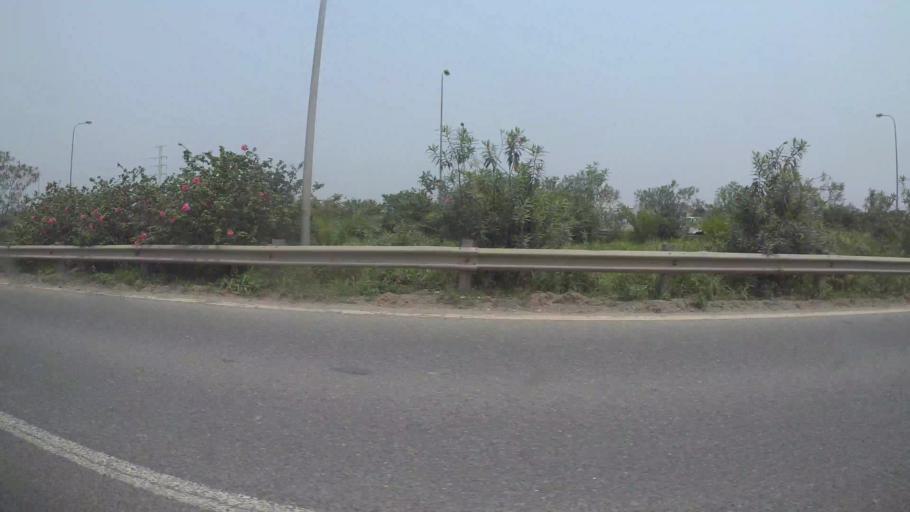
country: VN
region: Ha Noi
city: Quoc Oai
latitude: 21.0027
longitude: 105.6590
